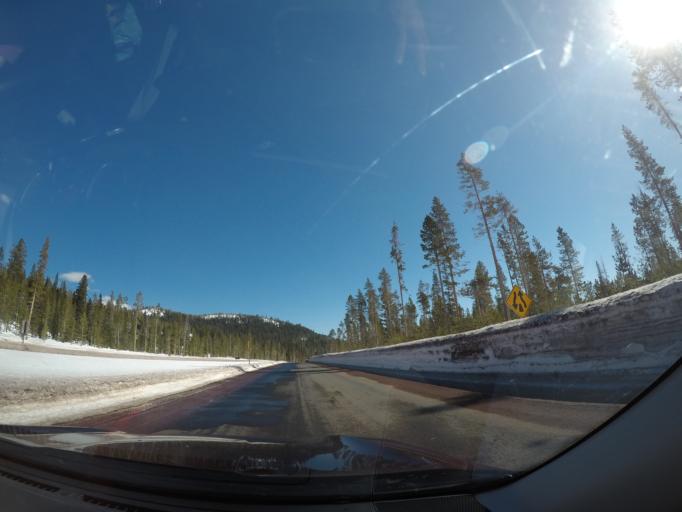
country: US
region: Oregon
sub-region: Deschutes County
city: Sunriver
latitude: 43.9827
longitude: -121.6104
